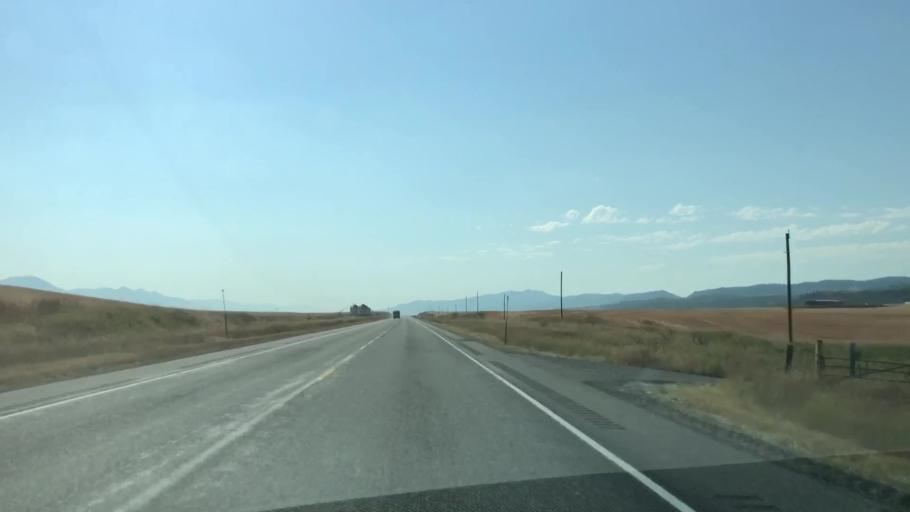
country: US
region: Idaho
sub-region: Teton County
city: Victor
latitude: 43.5213
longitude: -111.4923
